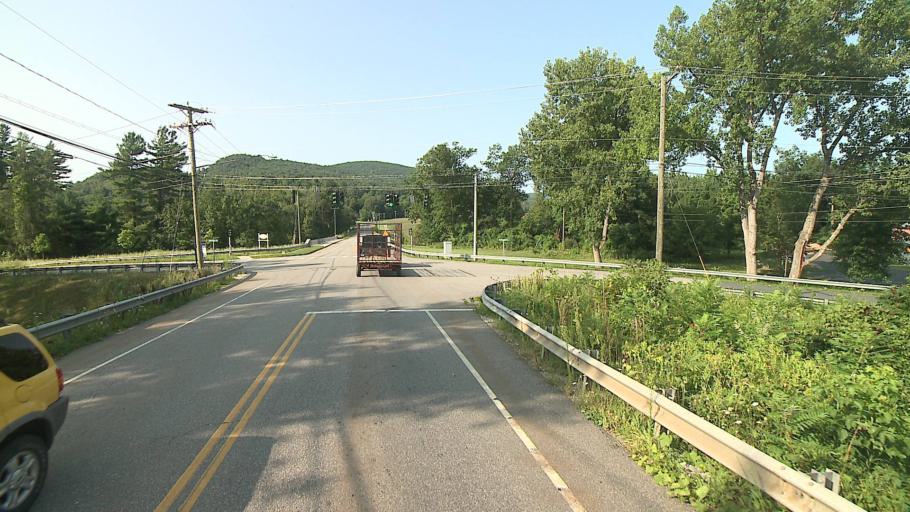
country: US
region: Connecticut
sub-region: Litchfield County
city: Canaan
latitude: 41.9354
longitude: -73.3609
